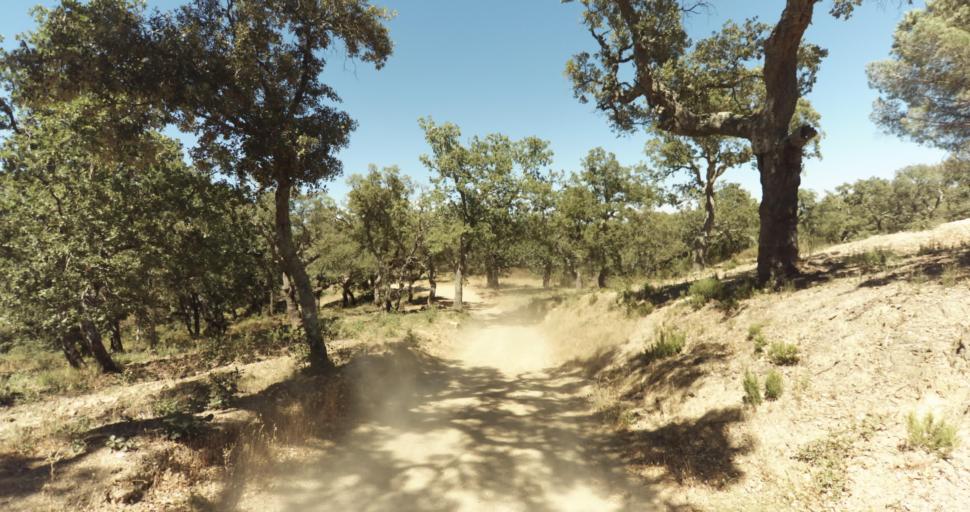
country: FR
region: Provence-Alpes-Cote d'Azur
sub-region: Departement du Var
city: Gassin
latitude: 43.2467
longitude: 6.5617
